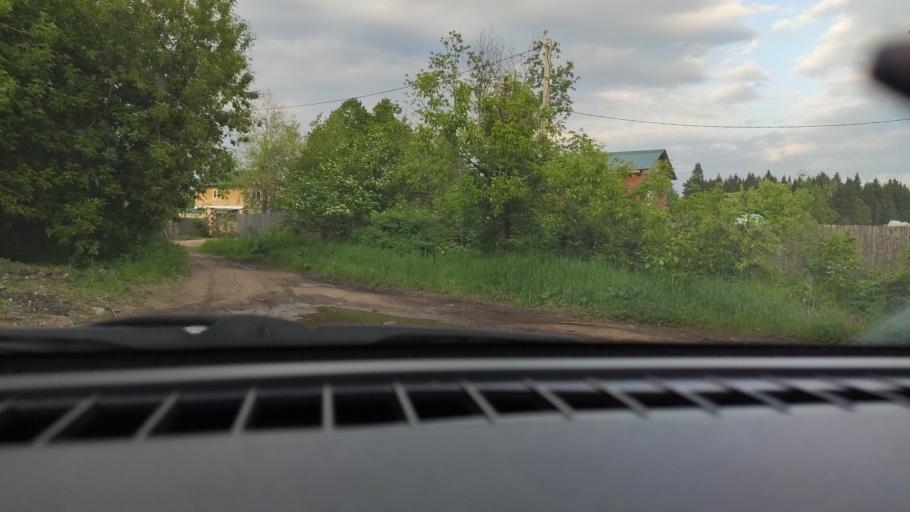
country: RU
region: Perm
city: Froly
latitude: 57.9500
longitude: 56.2817
